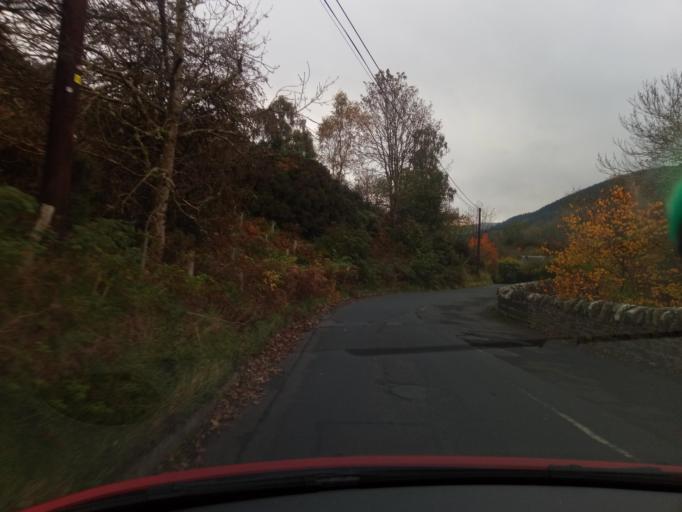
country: GB
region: Scotland
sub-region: The Scottish Borders
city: Galashiels
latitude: 55.6115
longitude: -2.8767
